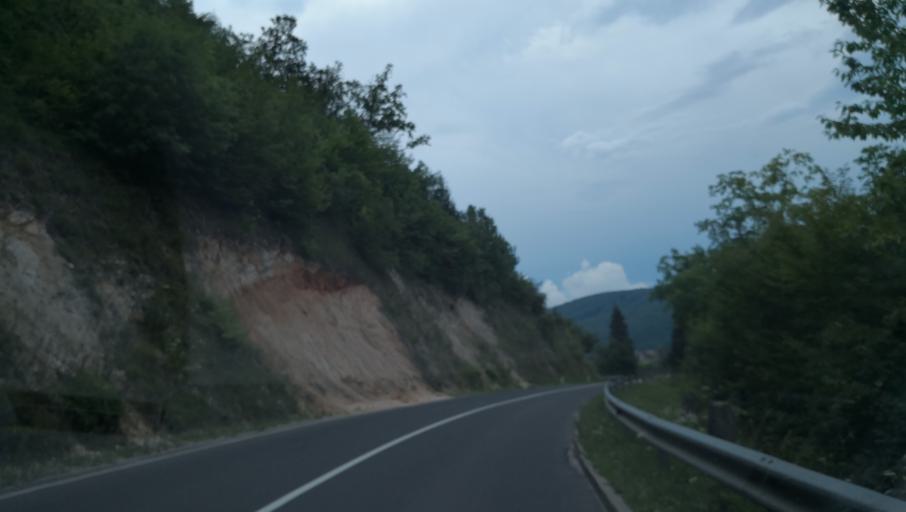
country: SI
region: Zuzemberk
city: Zuzemberk
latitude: 45.8454
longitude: 14.9058
